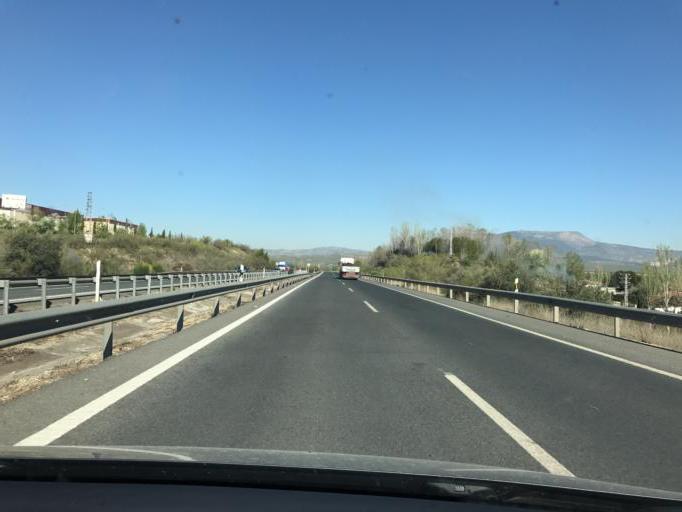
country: ES
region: Andalusia
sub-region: Provincia de Granada
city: Lachar
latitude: 37.1913
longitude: -3.8369
